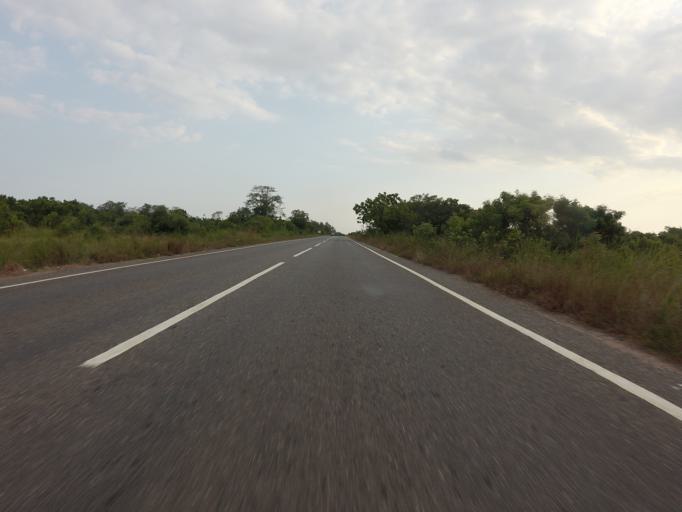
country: GH
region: Volta
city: Ho
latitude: 6.1148
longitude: 0.5183
